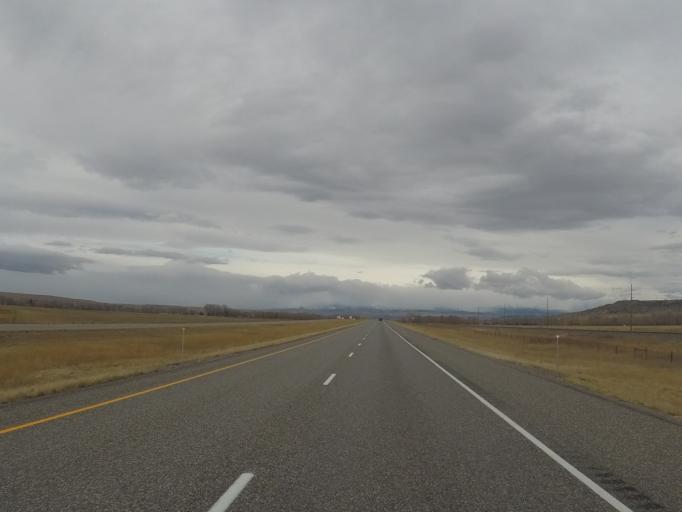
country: US
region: Montana
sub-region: Sweet Grass County
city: Big Timber
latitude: 45.7853
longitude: -109.8158
